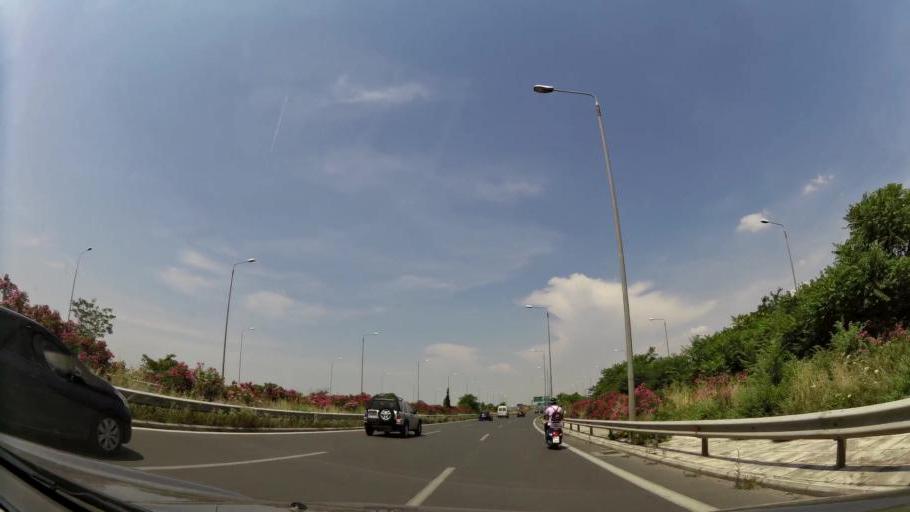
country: GR
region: Central Macedonia
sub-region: Nomos Thessalonikis
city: Menemeni
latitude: 40.6506
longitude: 22.9059
